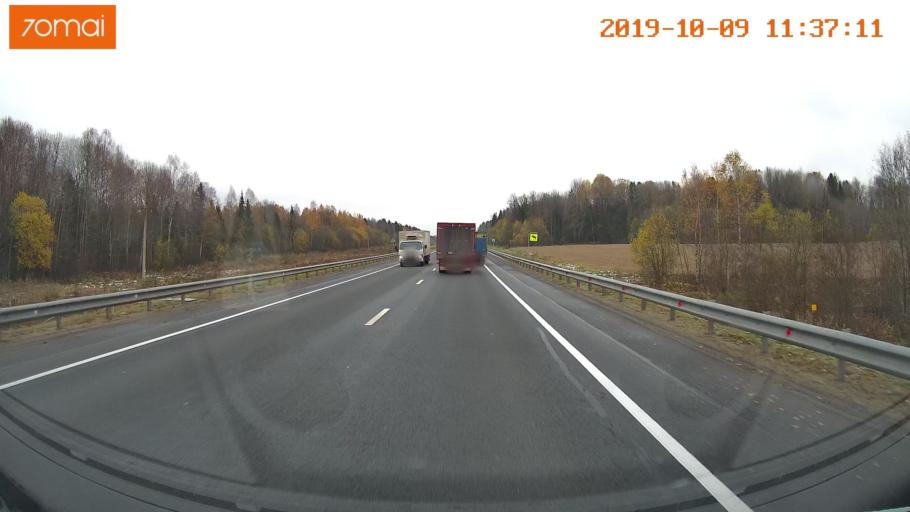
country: RU
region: Vologda
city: Gryazovets
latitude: 58.9820
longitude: 40.1436
